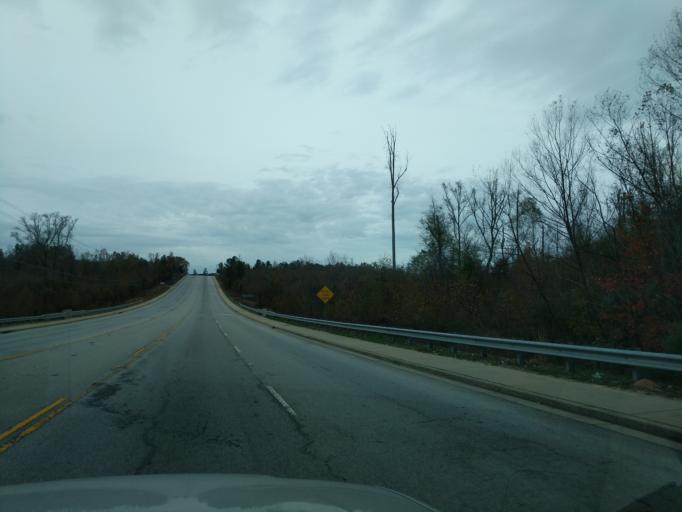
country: US
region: South Carolina
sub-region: Newberry County
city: Newberry
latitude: 34.3243
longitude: -81.6116
